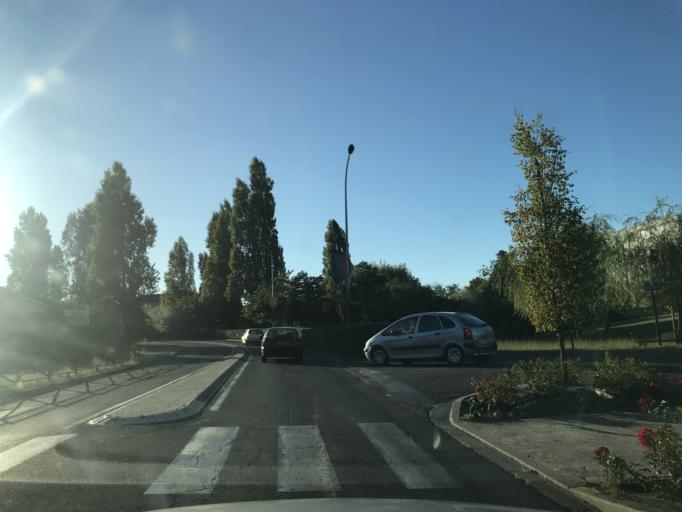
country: FR
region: Aquitaine
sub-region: Departement de la Gironde
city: Mouliets-et-Villemartin
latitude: 44.8556
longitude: -0.0453
